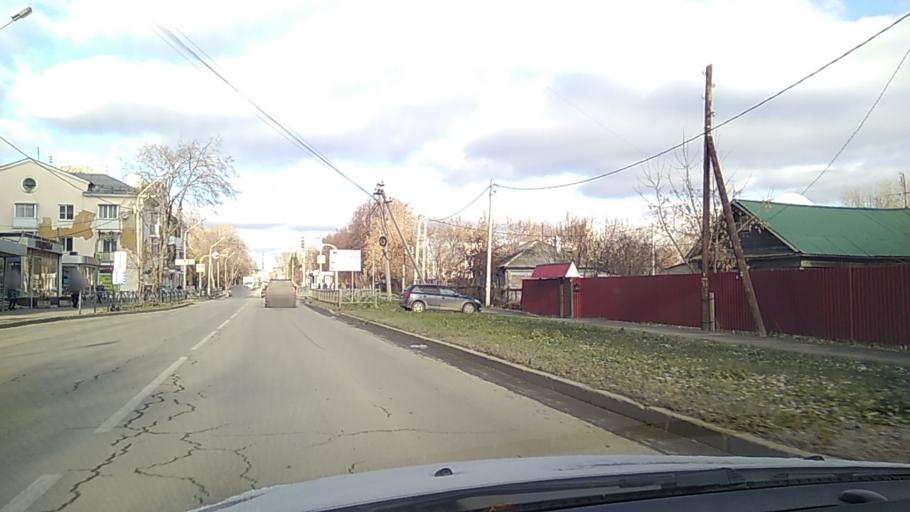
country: RU
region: Sverdlovsk
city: Sovkhoznyy
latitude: 56.7528
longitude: 60.6225
